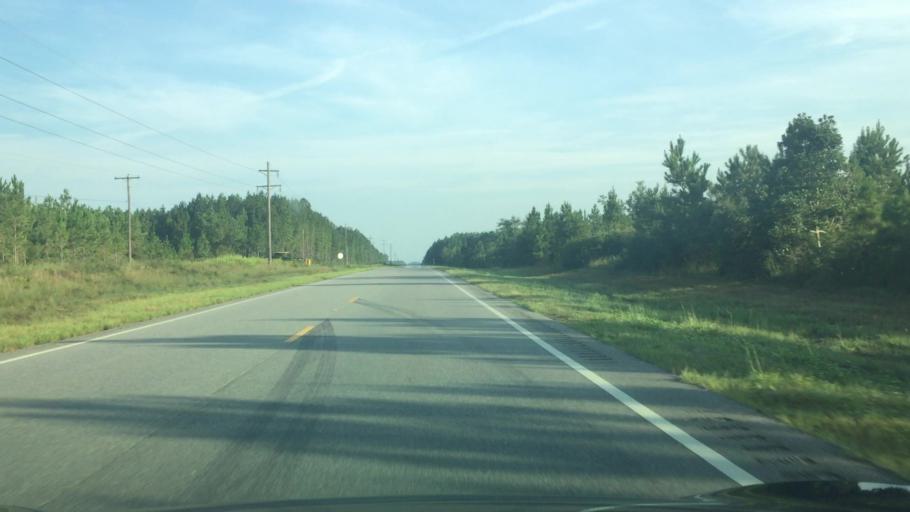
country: US
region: Alabama
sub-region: Covington County
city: Florala
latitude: 31.0254
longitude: -86.3670
